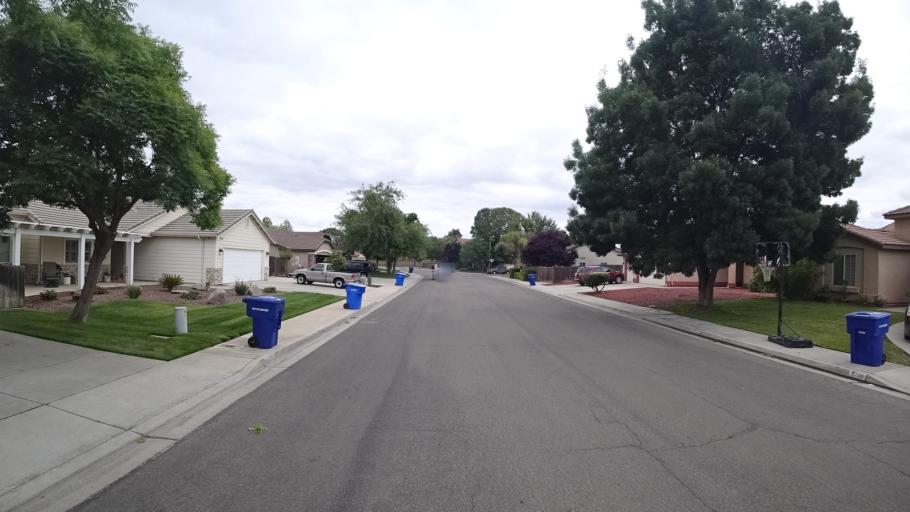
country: US
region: California
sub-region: Kings County
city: Armona
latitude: 36.3334
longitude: -119.6806
